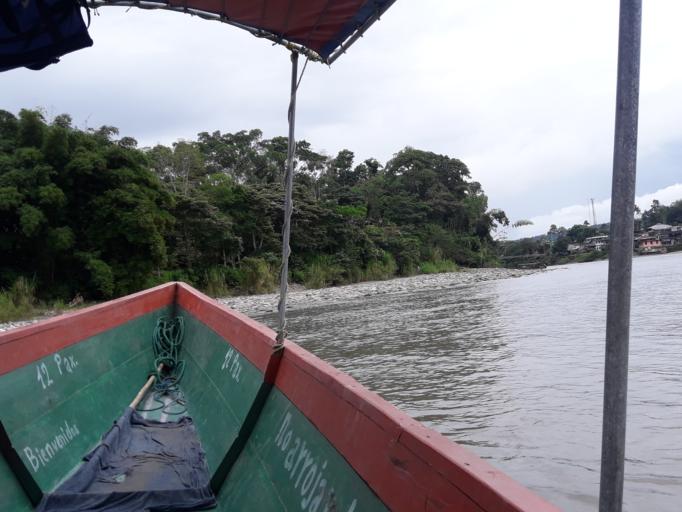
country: EC
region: Napo
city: Tena
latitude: -1.0369
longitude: -77.6621
